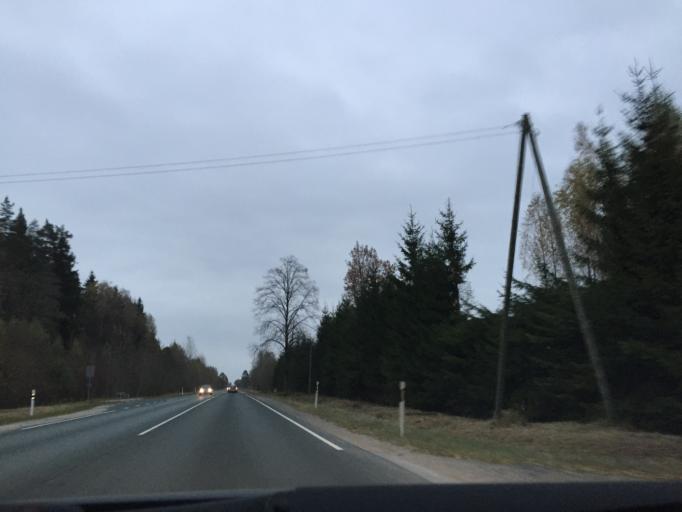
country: LV
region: Ozolnieku
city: Ozolnieki
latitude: 56.7153
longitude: 23.8355
